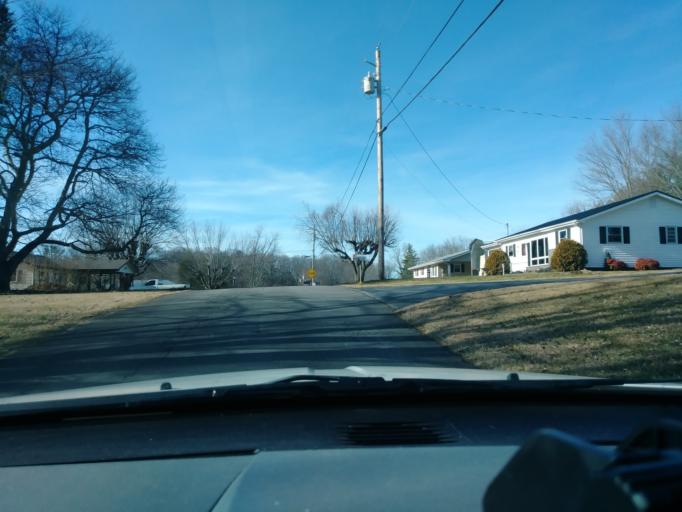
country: US
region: Tennessee
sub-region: Greene County
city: Greeneville
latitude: 36.1280
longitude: -82.8657
